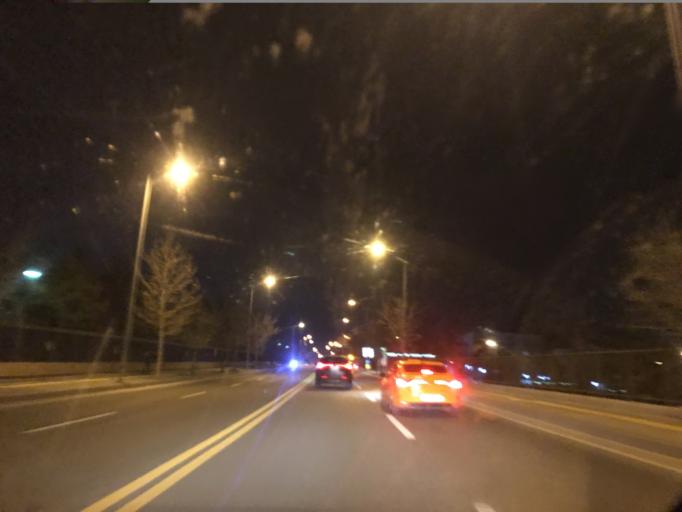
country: TR
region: Ankara
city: Cankaya
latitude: 39.8829
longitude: 32.8668
